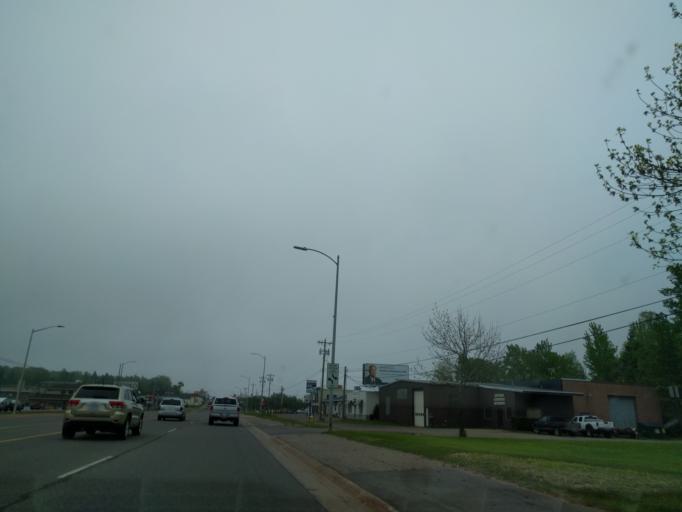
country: US
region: Michigan
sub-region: Marquette County
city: Trowbridge Park
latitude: 46.5458
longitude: -87.4242
